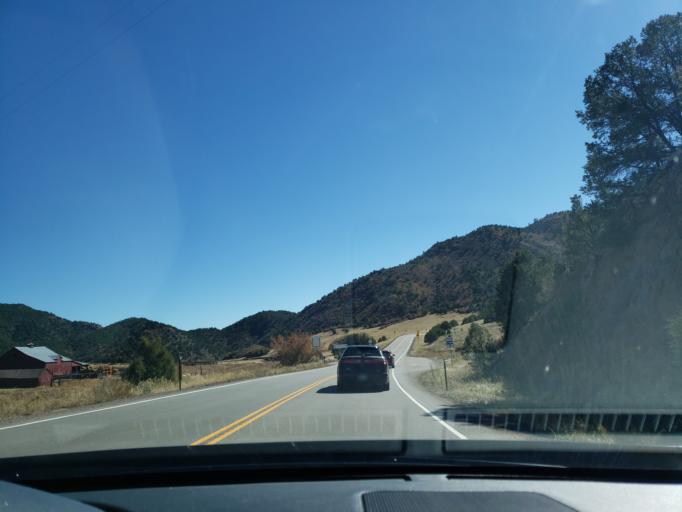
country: US
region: Colorado
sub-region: Fremont County
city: Canon City
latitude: 38.5855
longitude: -105.4181
